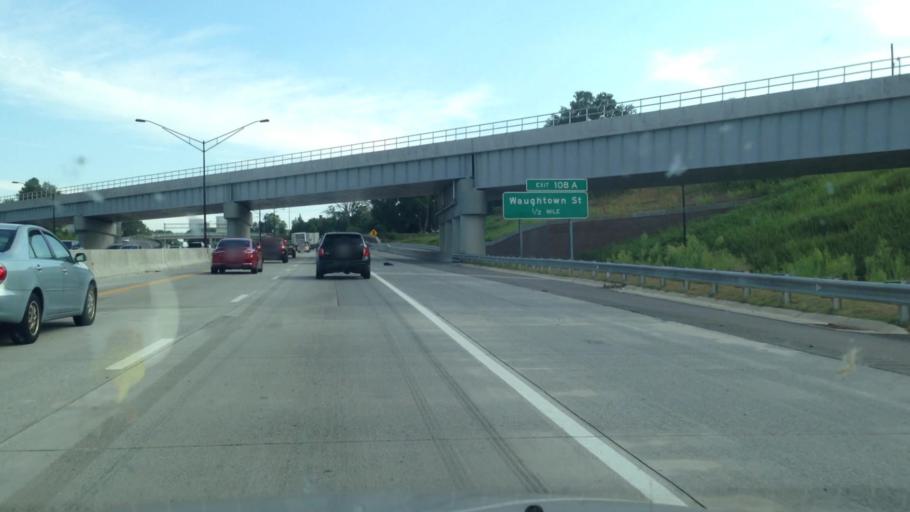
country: US
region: North Carolina
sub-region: Forsyth County
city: Winston-Salem
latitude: 36.0830
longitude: -80.2297
